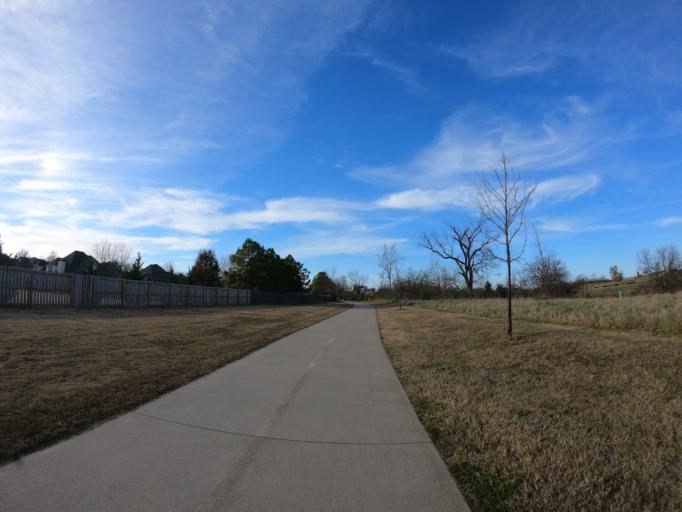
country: US
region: Arkansas
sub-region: Benton County
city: Lowell
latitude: 36.2926
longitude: -94.1741
